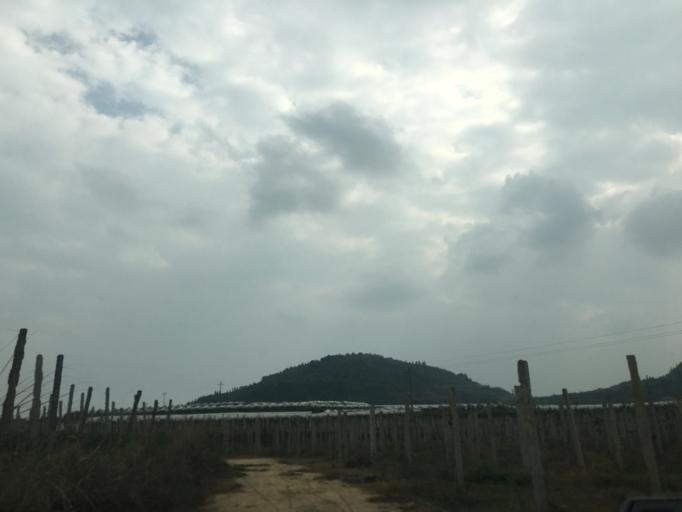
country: CN
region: Guangxi Zhuangzu Zizhiqu
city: Xinzhou
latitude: 25.4860
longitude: 105.6516
